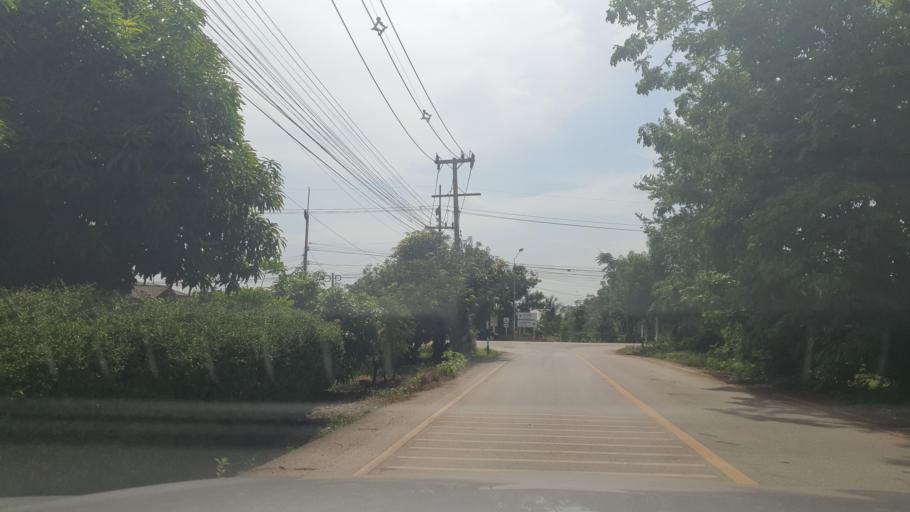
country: TH
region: Sukhothai
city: Si Samrong
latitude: 17.1418
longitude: 99.8243
